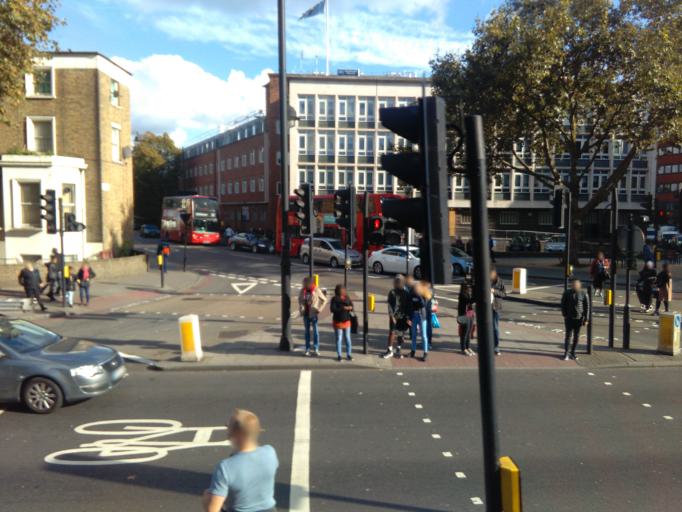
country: GB
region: England
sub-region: Greater London
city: Brixton
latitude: 51.4647
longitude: -0.1141
